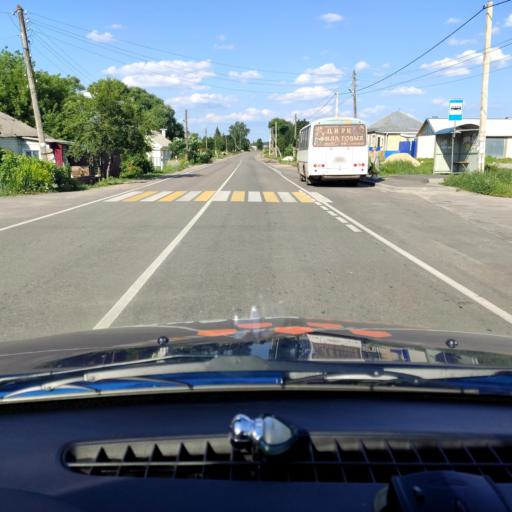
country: RU
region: Voronezj
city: Devitsa
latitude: 51.6401
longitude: 38.9486
